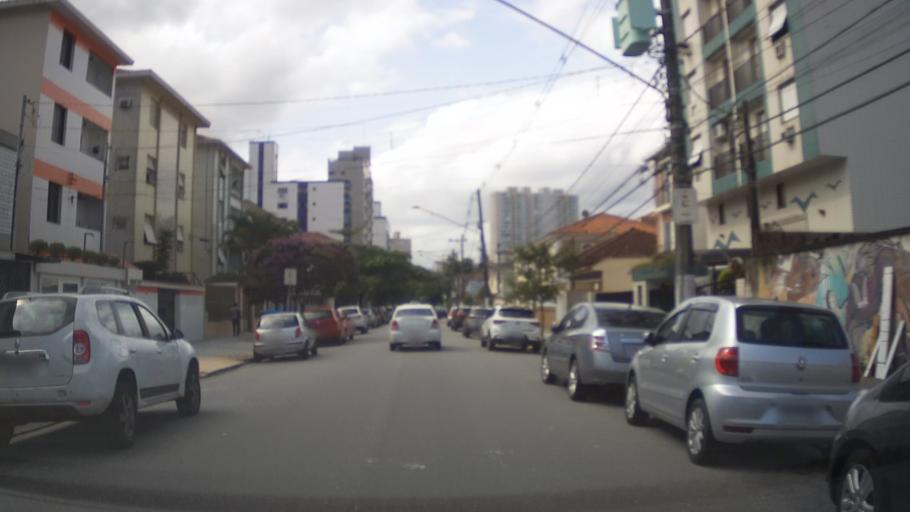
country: BR
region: Sao Paulo
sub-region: Santos
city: Santos
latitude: -23.9603
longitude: -46.3369
